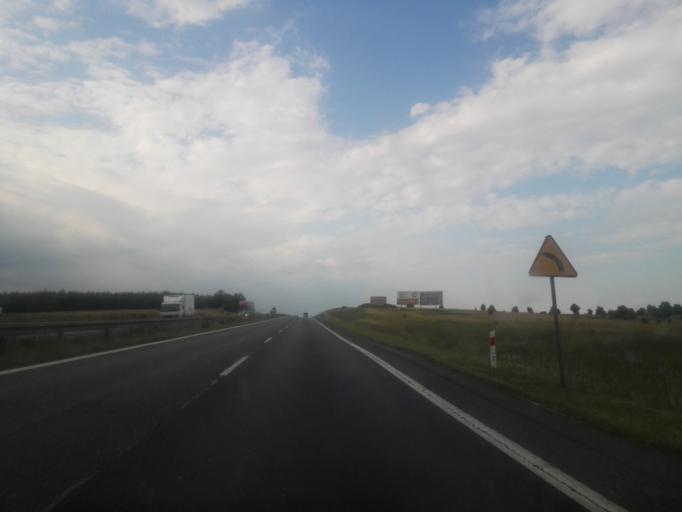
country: PL
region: Silesian Voivodeship
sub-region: Powiat myszkowski
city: Kozieglowy
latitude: 50.5790
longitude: 19.1634
